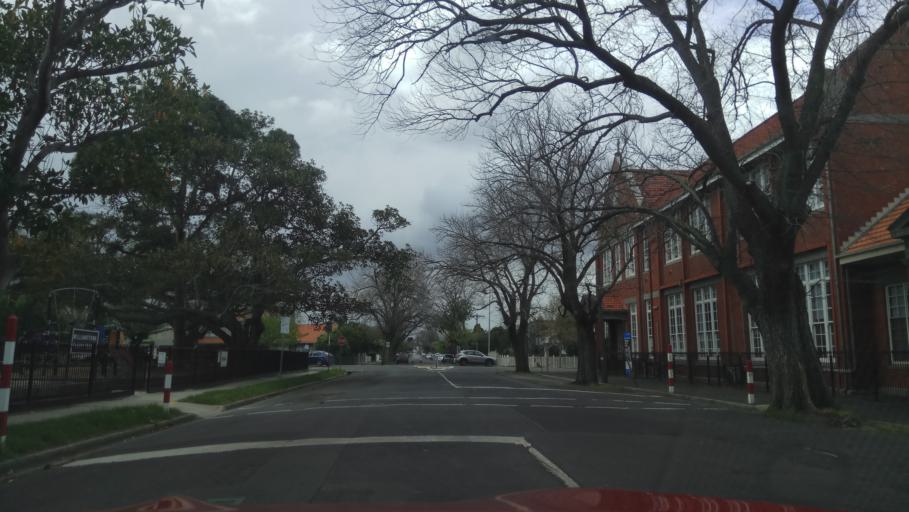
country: AU
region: Victoria
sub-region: Hobsons Bay
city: Williamstown
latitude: -37.8640
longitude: 144.9007
